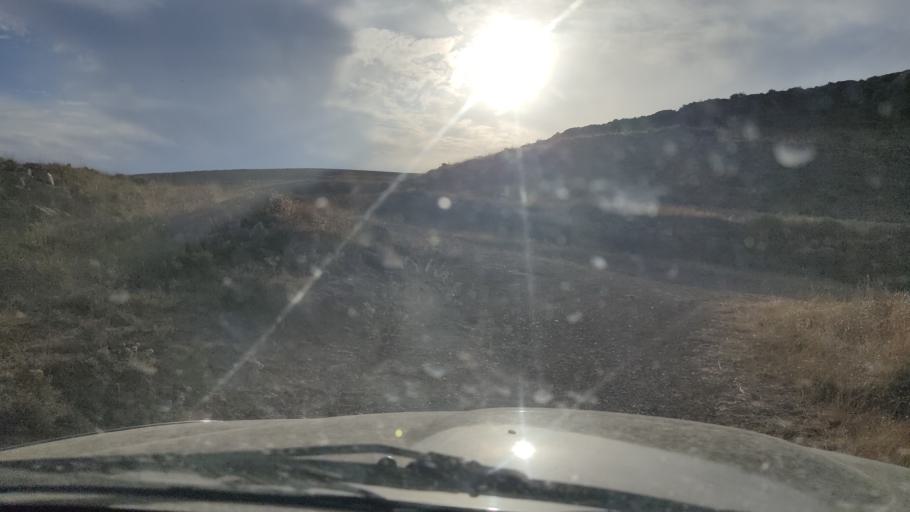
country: ES
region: Aragon
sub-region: Provincia de Teruel
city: Monforte de Moyuela
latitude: 41.0557
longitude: -0.9744
